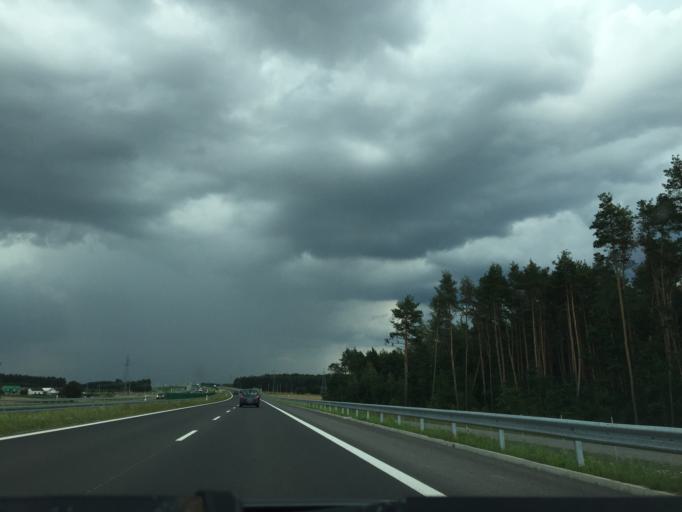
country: PL
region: Masovian Voivodeship
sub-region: Powiat szydlowiecki
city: Oronsko
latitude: 51.2847
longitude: 20.9720
